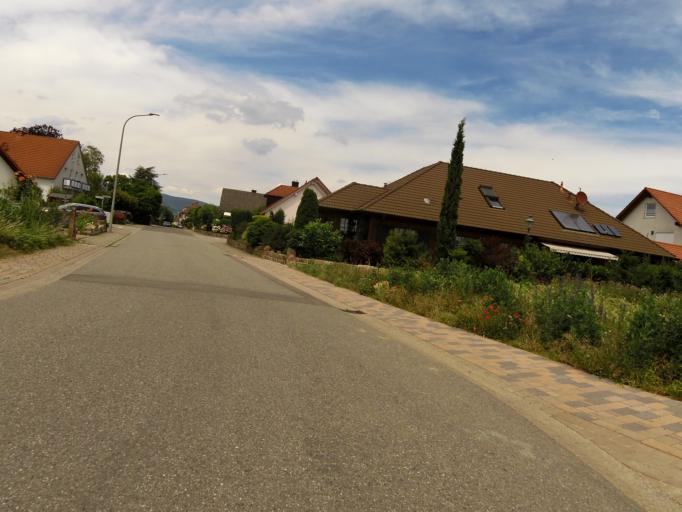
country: DE
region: Rheinland-Pfalz
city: Edesheim
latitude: 49.2601
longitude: 8.1360
